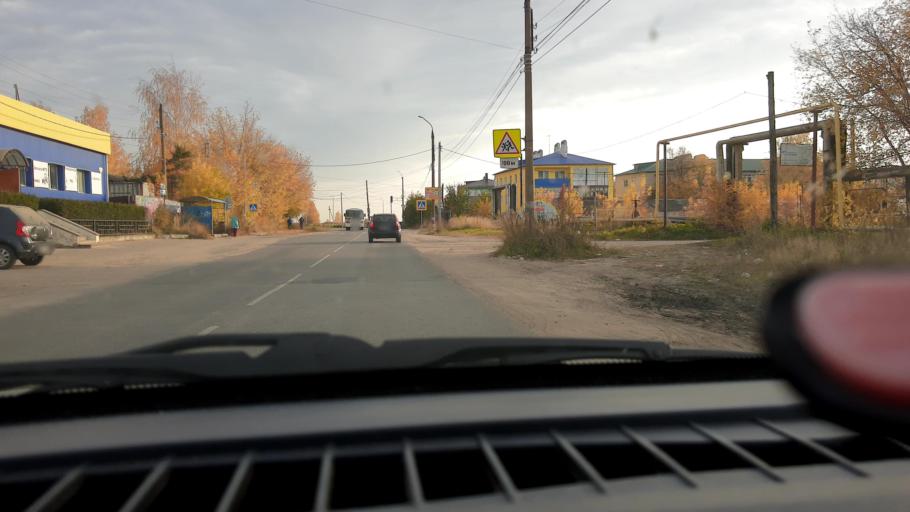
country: RU
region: Nizjnij Novgorod
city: Gorodets
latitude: 56.6416
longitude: 43.4896
